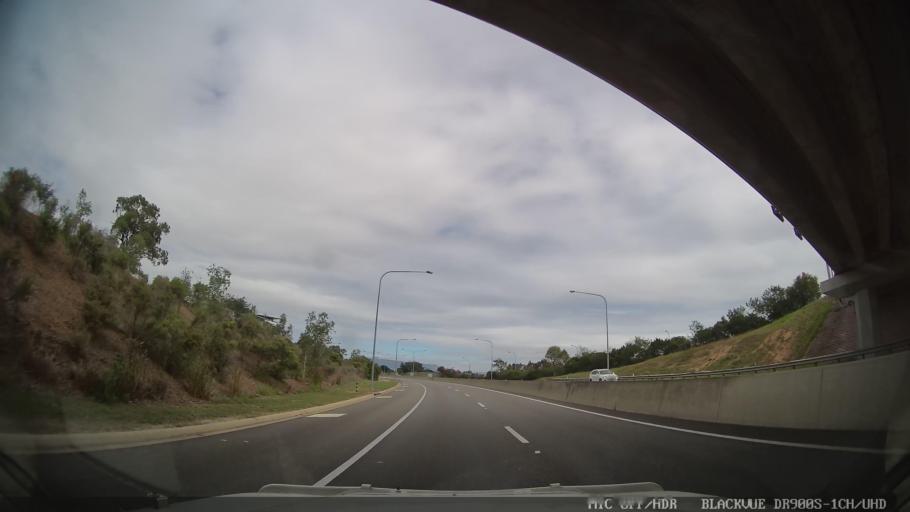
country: AU
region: Queensland
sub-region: Townsville
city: Bohle Plains
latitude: -19.3216
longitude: 146.7422
